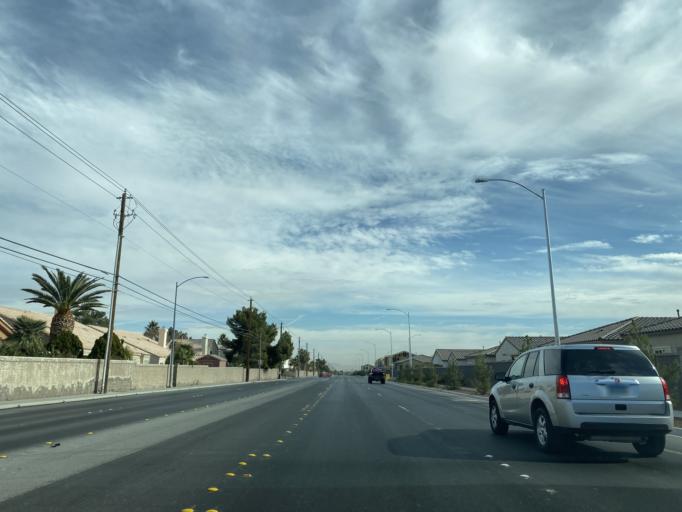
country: US
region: Nevada
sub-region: Clark County
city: North Las Vegas
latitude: 36.2467
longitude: -115.1681
